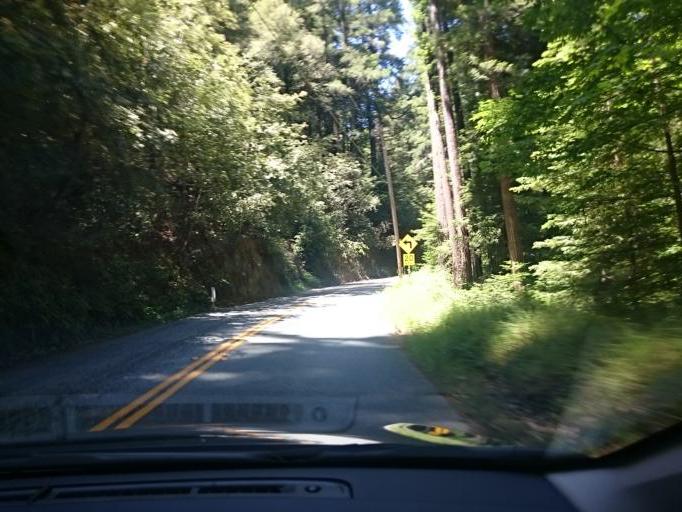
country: US
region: California
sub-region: Santa Cruz County
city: Felton
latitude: 37.0487
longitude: -122.0882
